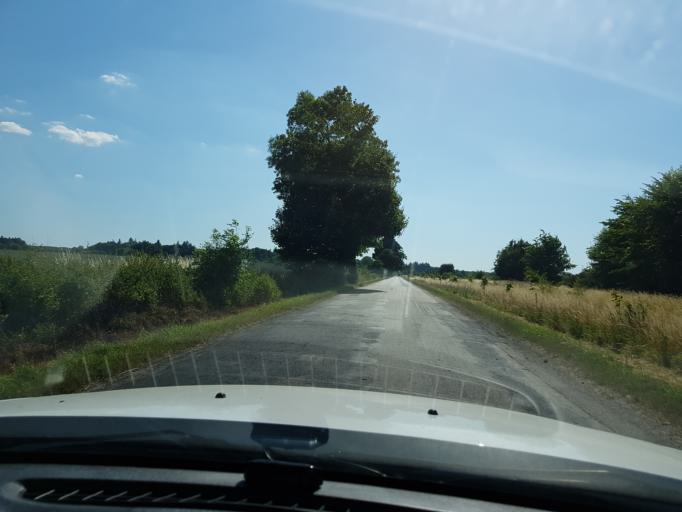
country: PL
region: West Pomeranian Voivodeship
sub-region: Powiat bialogardzki
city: Karlino
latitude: 53.9387
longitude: 15.8358
